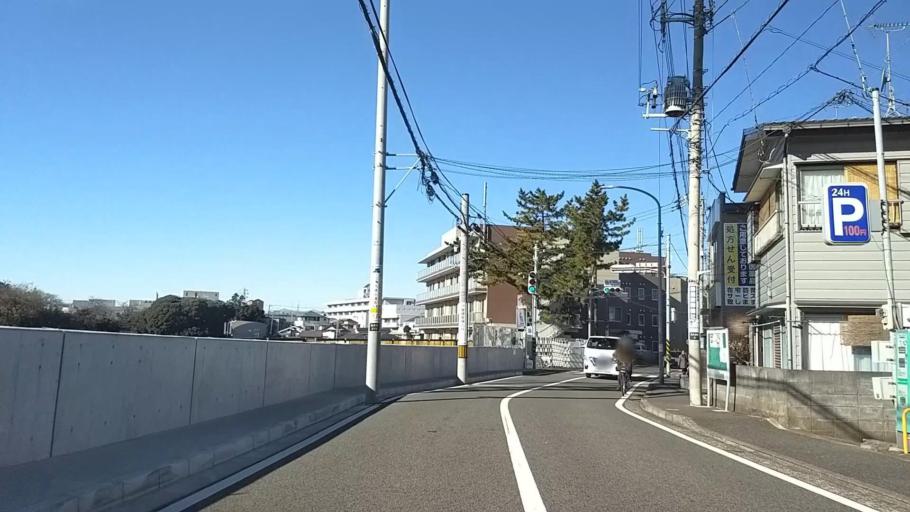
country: JP
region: Kanagawa
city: Yokohama
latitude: 35.4430
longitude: 139.6049
